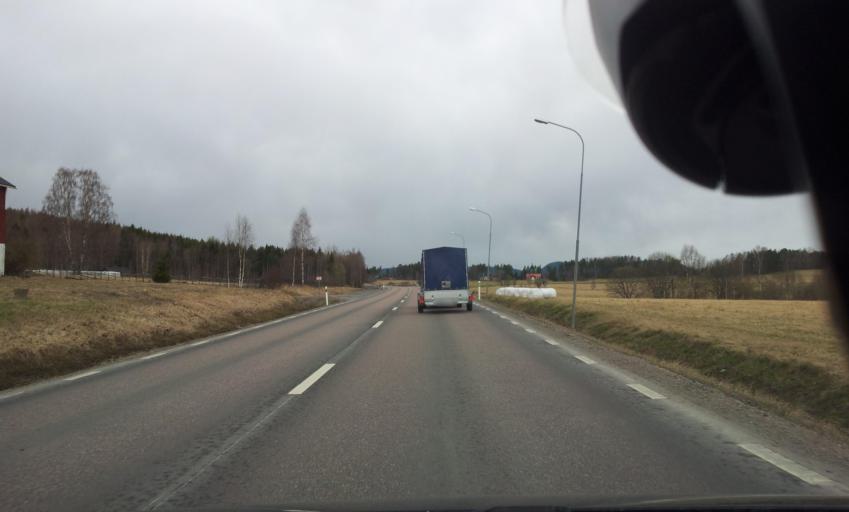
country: SE
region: Gaevleborg
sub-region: Ljusdals Kommun
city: Ljusdal
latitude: 61.8228
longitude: 16.0516
